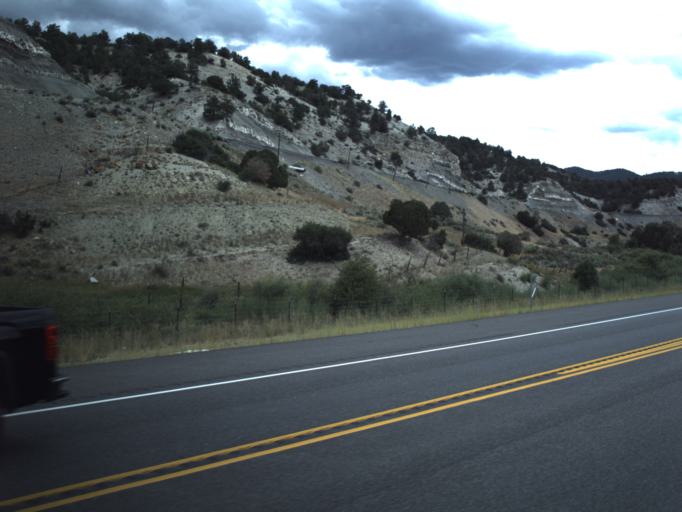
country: US
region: Utah
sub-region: Sanpete County
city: Fairview
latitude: 39.9481
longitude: -111.2145
